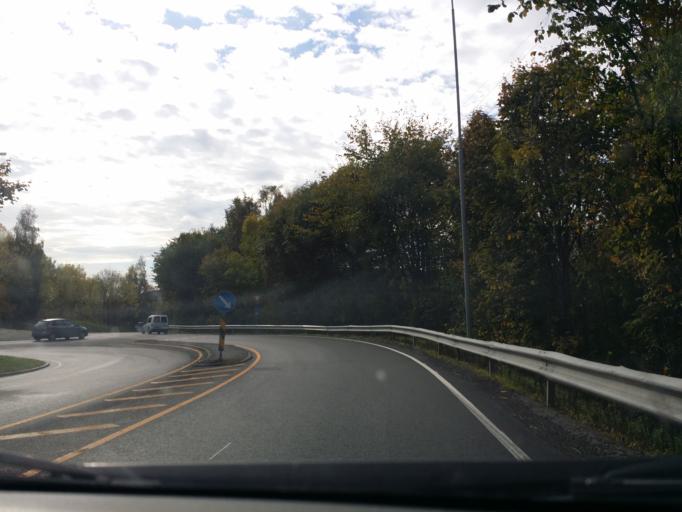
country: NO
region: Akershus
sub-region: Baerum
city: Sandvika
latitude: 59.9171
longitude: 10.4958
